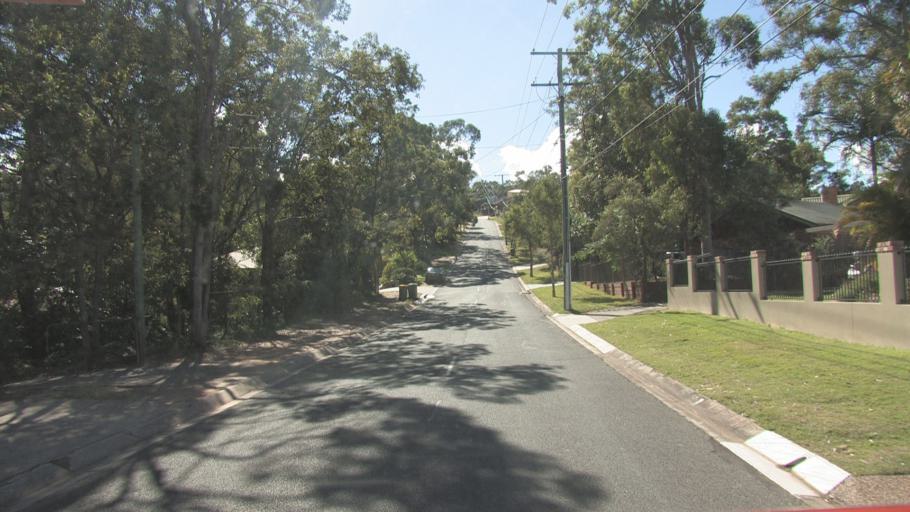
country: AU
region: Queensland
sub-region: Logan
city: Beenleigh
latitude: -27.6654
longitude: 153.1943
